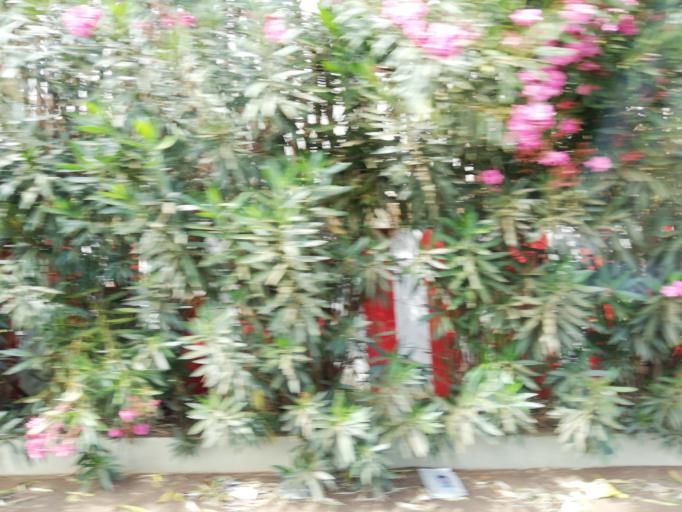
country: MU
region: Black River
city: Petite Riviere
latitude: -20.2145
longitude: 57.4588
